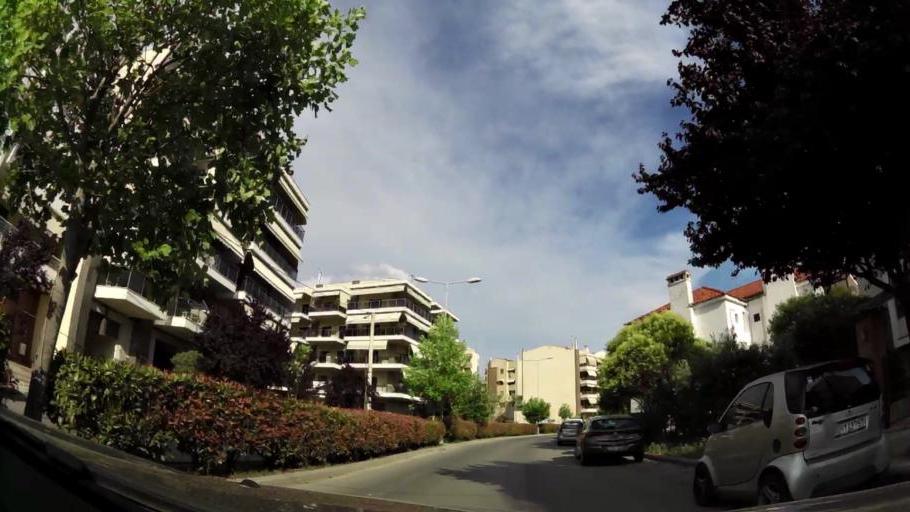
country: GR
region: Central Macedonia
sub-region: Nomos Thessalonikis
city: Kalamaria
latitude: 40.5757
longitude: 22.9643
